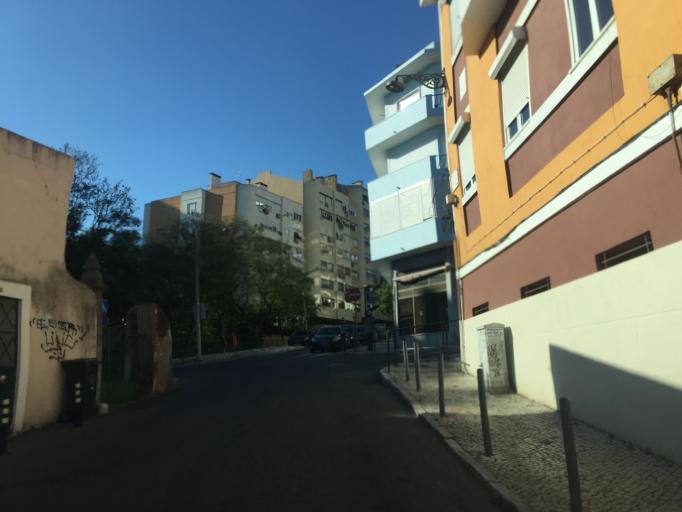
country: PT
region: Lisbon
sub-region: Odivelas
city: Pontinha
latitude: 38.7463
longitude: -9.1804
